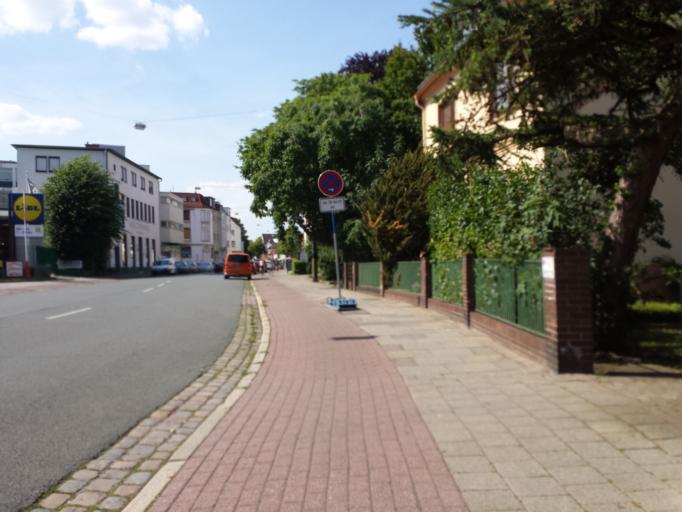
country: DE
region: Bremen
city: Bremen
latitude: 53.0855
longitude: 8.7647
